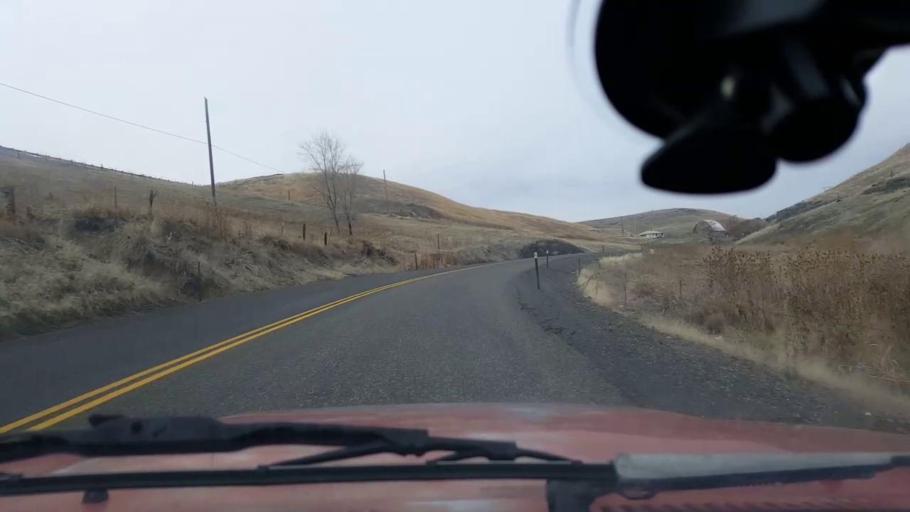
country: US
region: Washington
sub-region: Asotin County
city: Clarkston Heights-Vineland
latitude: 46.3840
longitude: -117.1364
